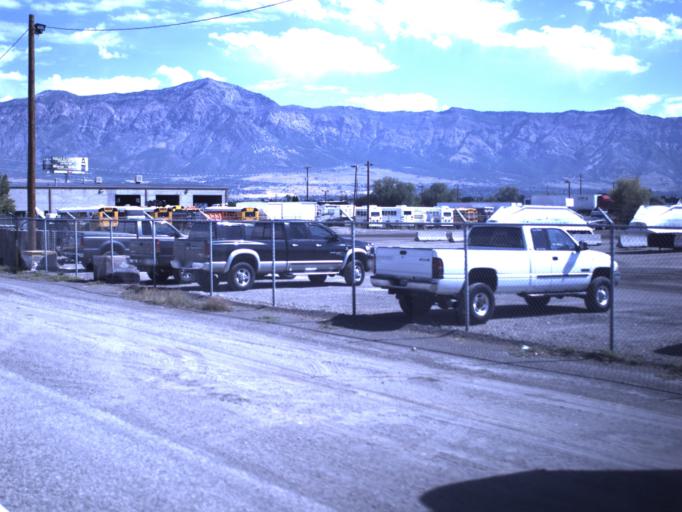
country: US
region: Utah
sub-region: Weber County
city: Farr West
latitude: 41.2756
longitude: -112.0281
